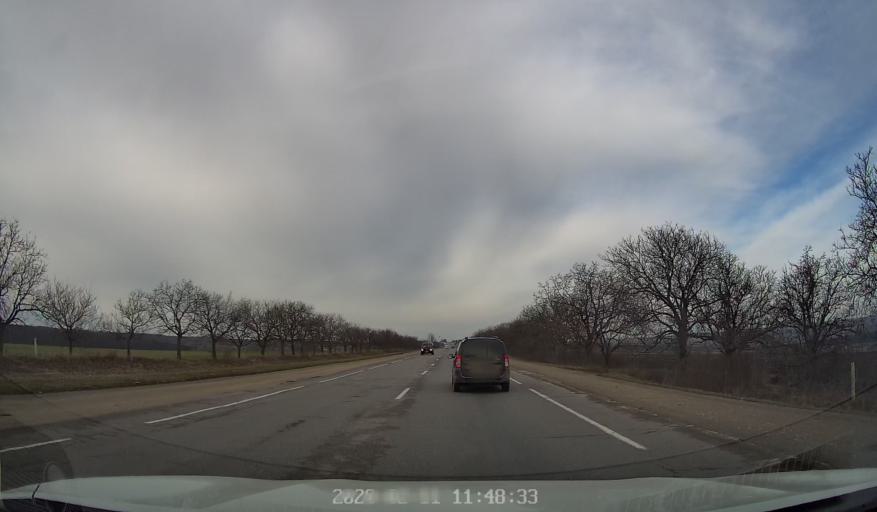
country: MD
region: Balti
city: Balti
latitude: 47.8395
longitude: 27.8021
